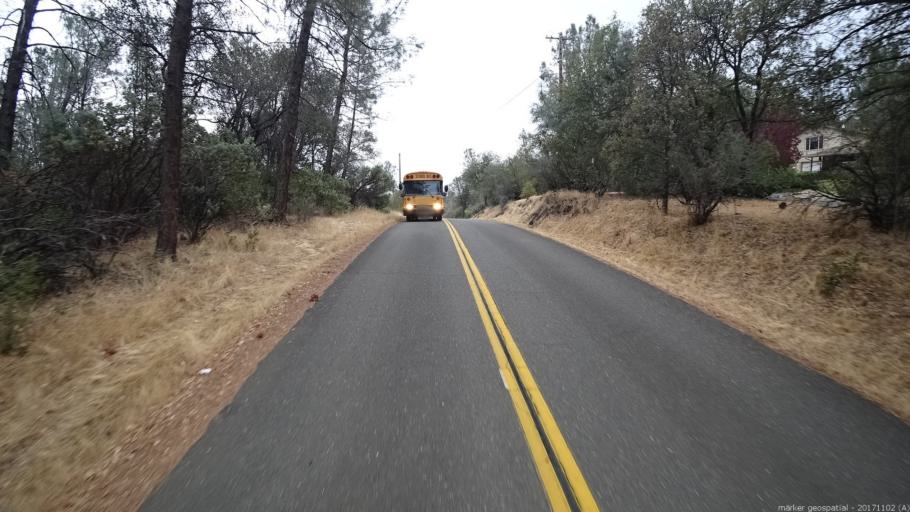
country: US
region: California
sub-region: Shasta County
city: Central Valley (historical)
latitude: 40.6582
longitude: -122.3988
